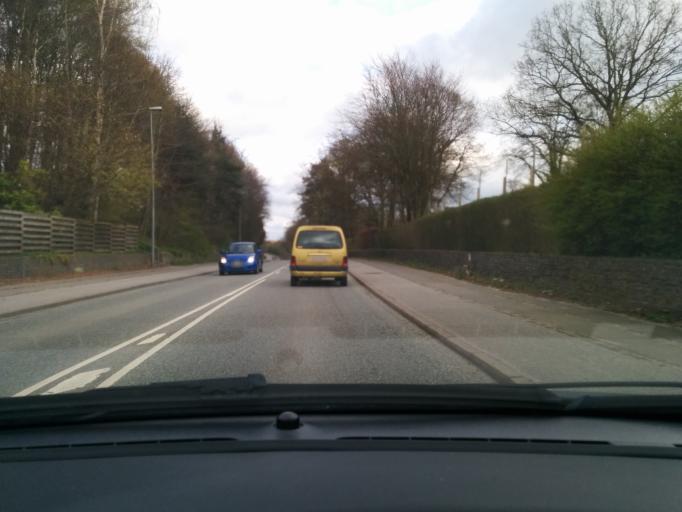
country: DK
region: Central Jutland
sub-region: Favrskov Kommune
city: Hadsten
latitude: 56.3256
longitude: 10.0607
